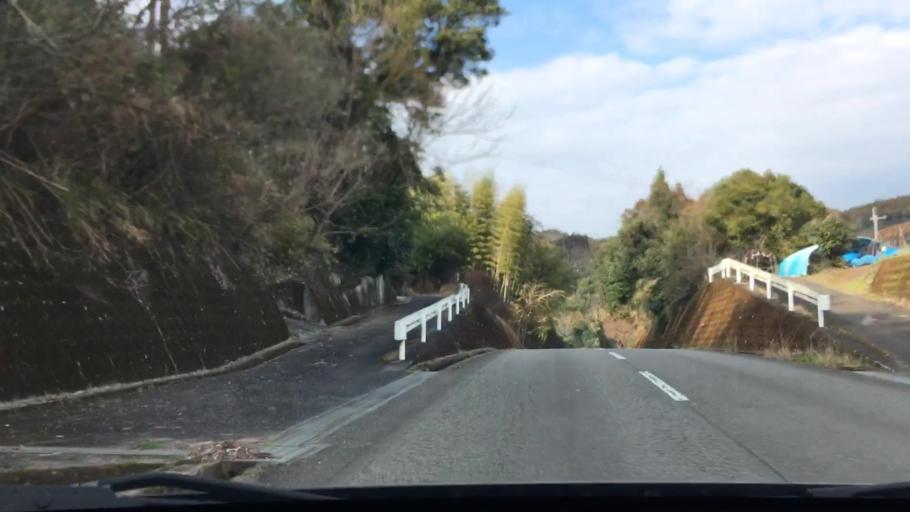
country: JP
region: Miyazaki
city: Nichinan
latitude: 31.5925
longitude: 131.3072
